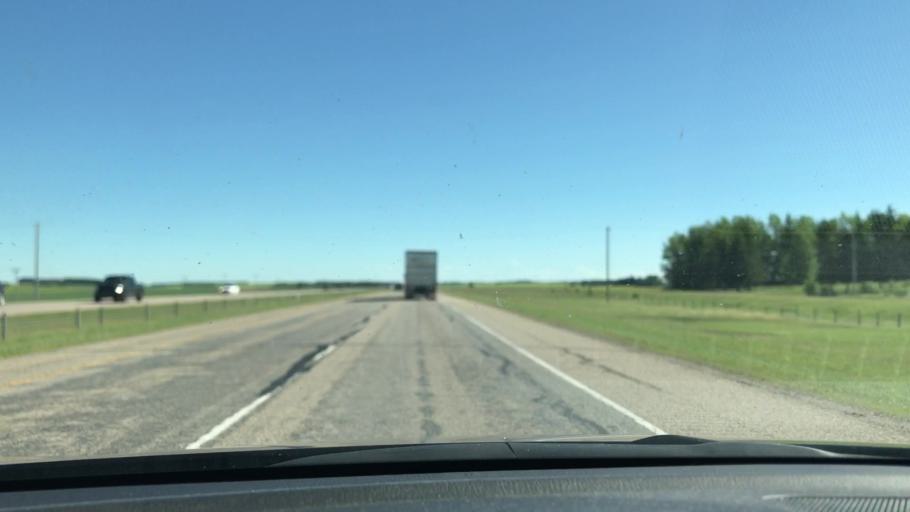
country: CA
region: Alberta
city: Olds
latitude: 51.8793
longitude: -114.0256
